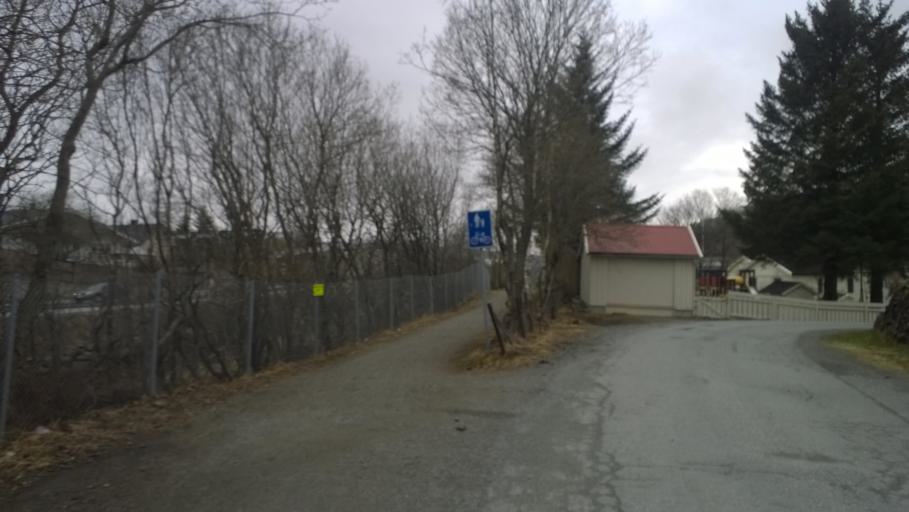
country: NO
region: Nordland
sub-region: Bodo
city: Lopsmarka
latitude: 67.2783
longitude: 14.4926
